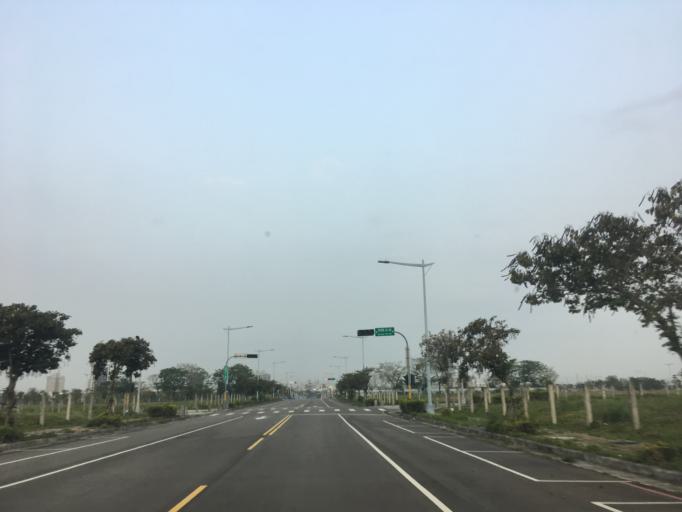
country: TW
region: Taiwan
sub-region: Taichung City
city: Taichung
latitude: 24.1967
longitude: 120.6729
